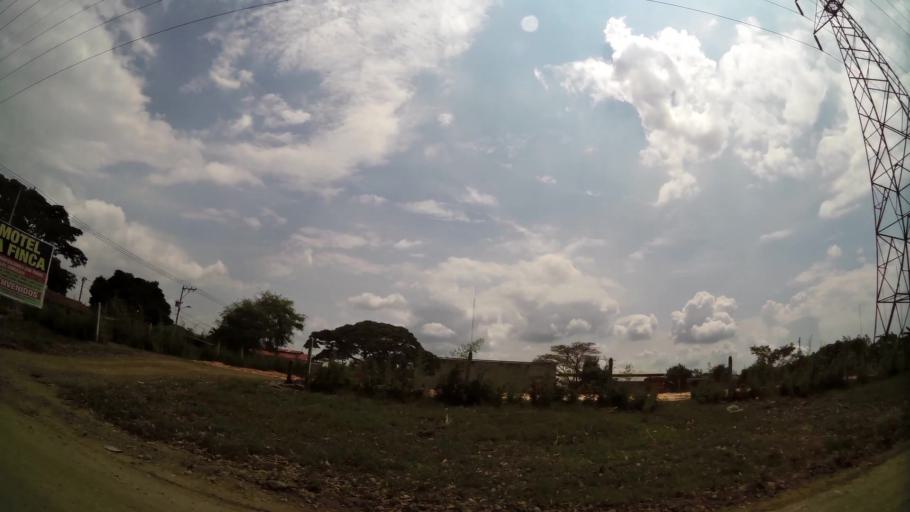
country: CO
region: Valle del Cauca
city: Cali
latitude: 3.4973
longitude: -76.4787
